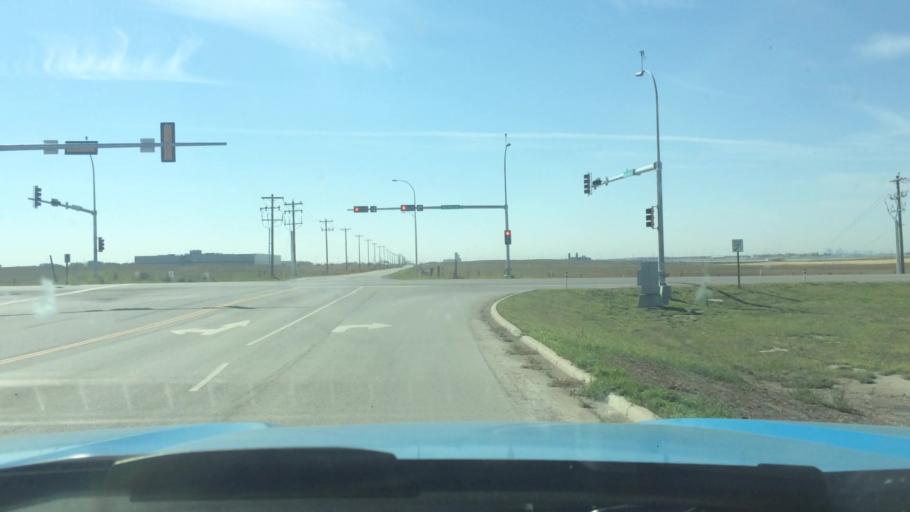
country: CA
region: Alberta
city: Airdrie
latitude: 51.2131
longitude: -113.9353
